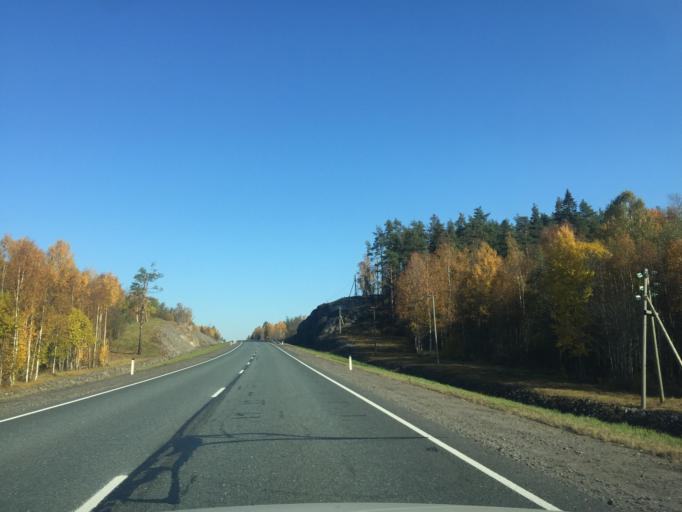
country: RU
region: Leningrad
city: Kuznechnoye
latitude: 61.3491
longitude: 29.8797
